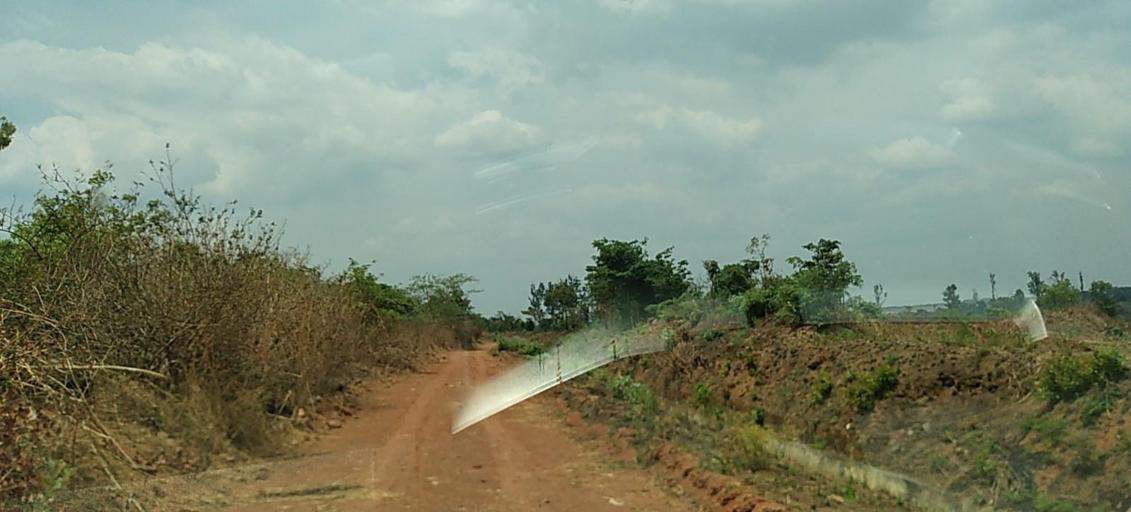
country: ZM
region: Copperbelt
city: Chililabombwe
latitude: -12.3643
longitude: 27.7982
